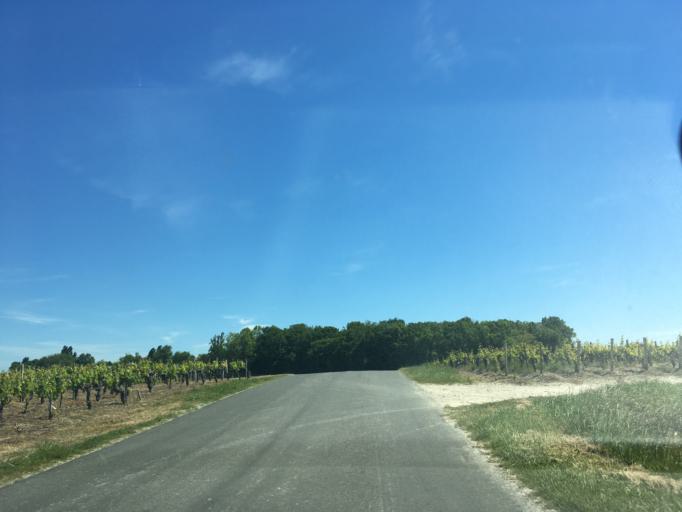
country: FR
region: Aquitaine
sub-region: Departement de la Gironde
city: Lesparre-Medoc
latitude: 45.3184
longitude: -0.8813
